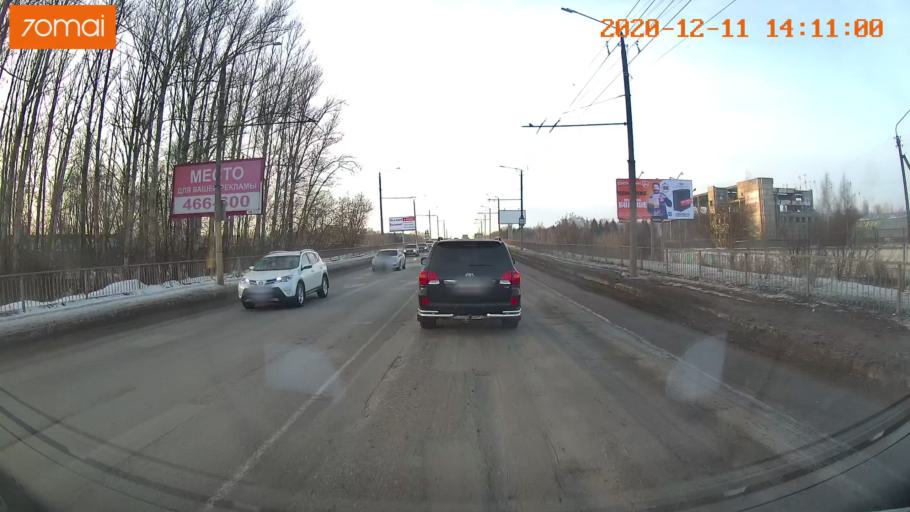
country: RU
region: Kostroma
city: Oktyabr'skiy
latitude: 57.7413
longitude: 40.9753
